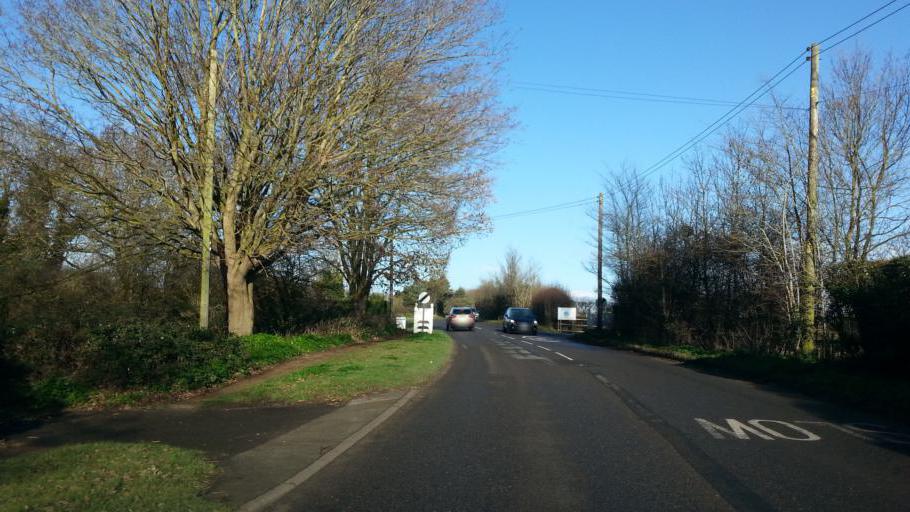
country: GB
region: England
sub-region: Suffolk
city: Saxmundham
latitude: 52.1743
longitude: 1.5012
